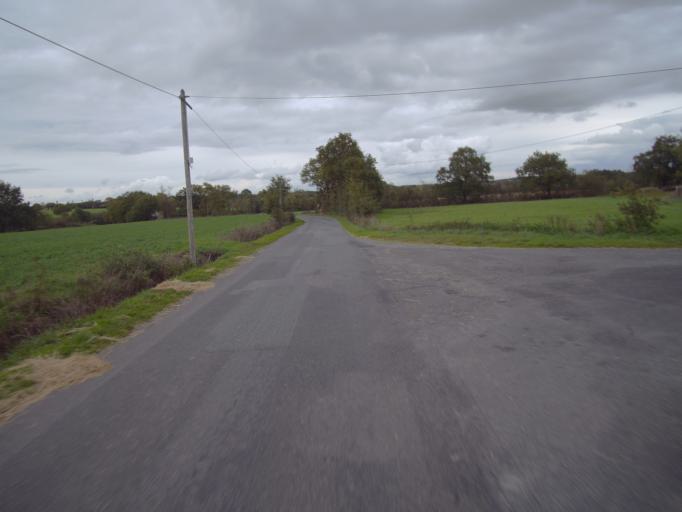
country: FR
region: Pays de la Loire
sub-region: Departement de la Loire-Atlantique
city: Remouille
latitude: 47.0242
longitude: -1.3821
